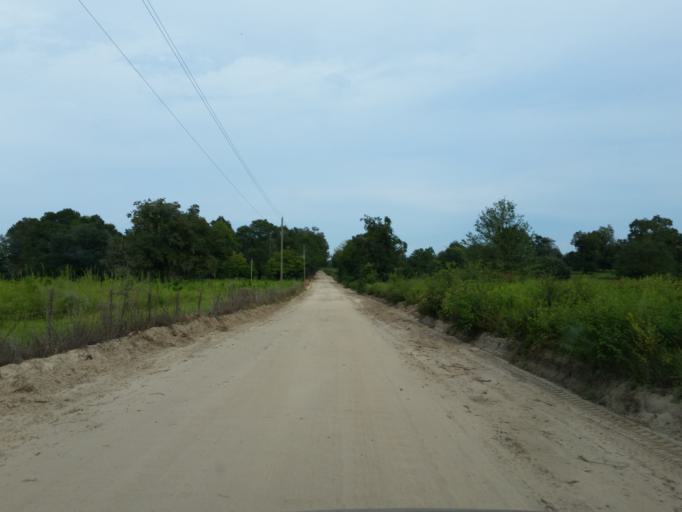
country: US
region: Florida
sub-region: Madison County
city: Madison
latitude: 30.5375
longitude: -83.2033
